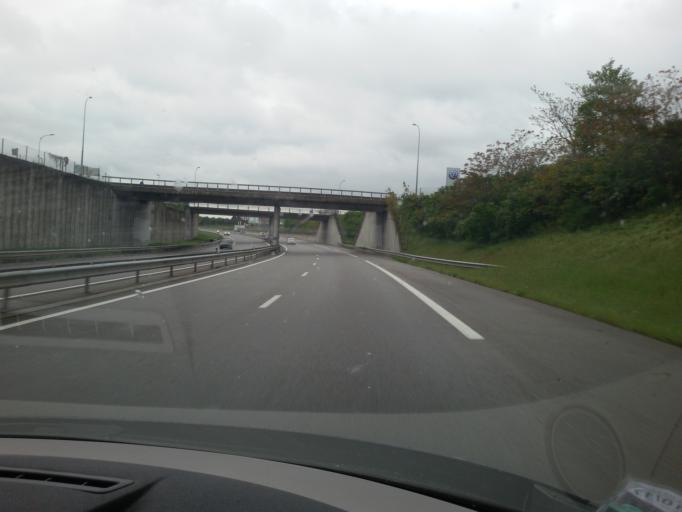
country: FR
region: Rhone-Alpes
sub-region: Departement de la Drome
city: Romans-sur-Isere
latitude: 45.0198
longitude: 5.0352
